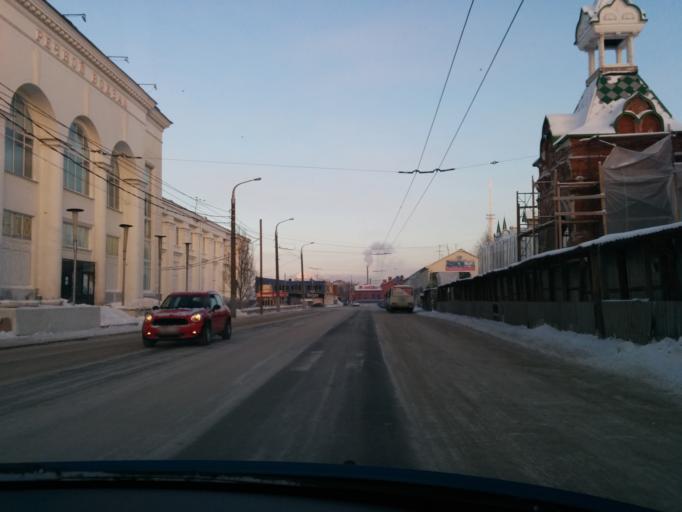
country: RU
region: Perm
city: Perm
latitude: 58.0202
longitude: 56.2510
